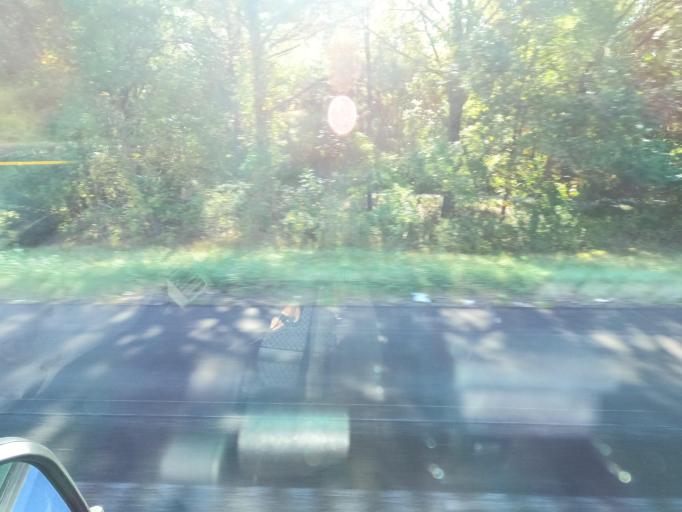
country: US
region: Tennessee
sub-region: Tipton County
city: Mason
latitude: 35.3374
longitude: -89.5431
